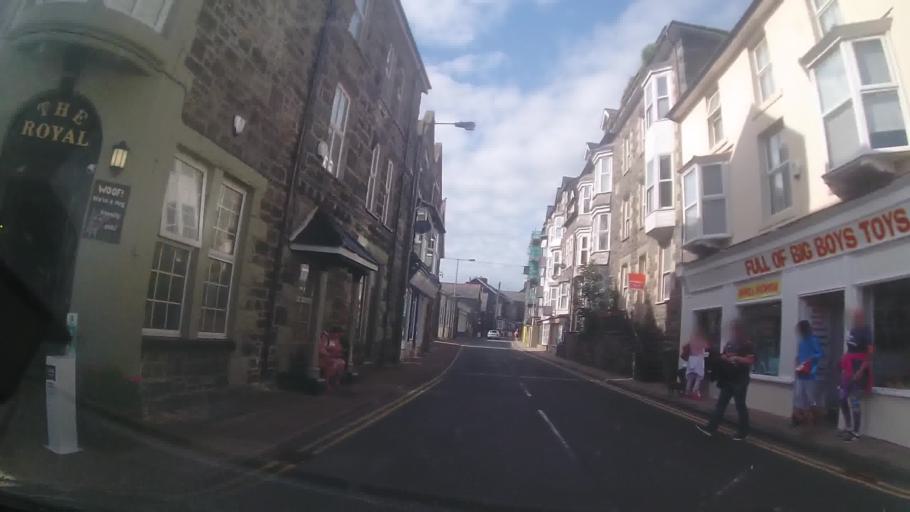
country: GB
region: Wales
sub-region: Gwynedd
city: Barmouth
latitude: 52.7235
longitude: -4.0562
